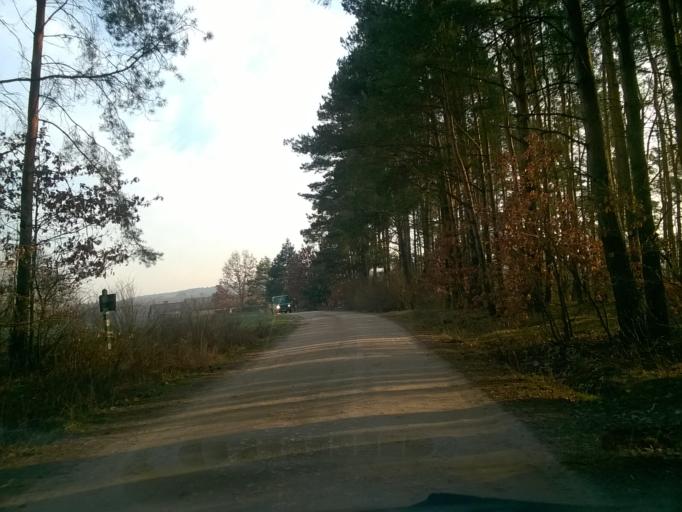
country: PL
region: Kujawsko-Pomorskie
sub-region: Powiat tucholski
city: Kesowo
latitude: 53.5037
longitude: 17.7046
